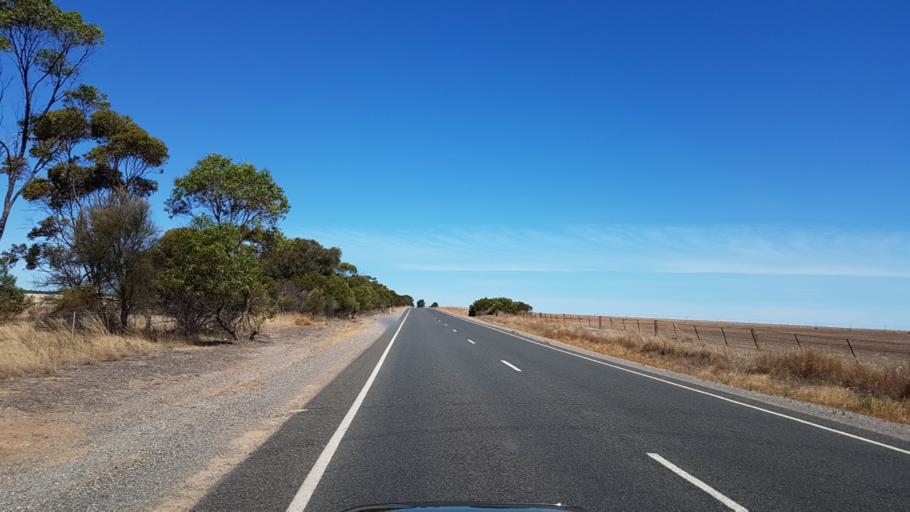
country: AU
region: South Australia
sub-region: Yorke Peninsula
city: Maitland
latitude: -34.3414
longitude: 137.6582
